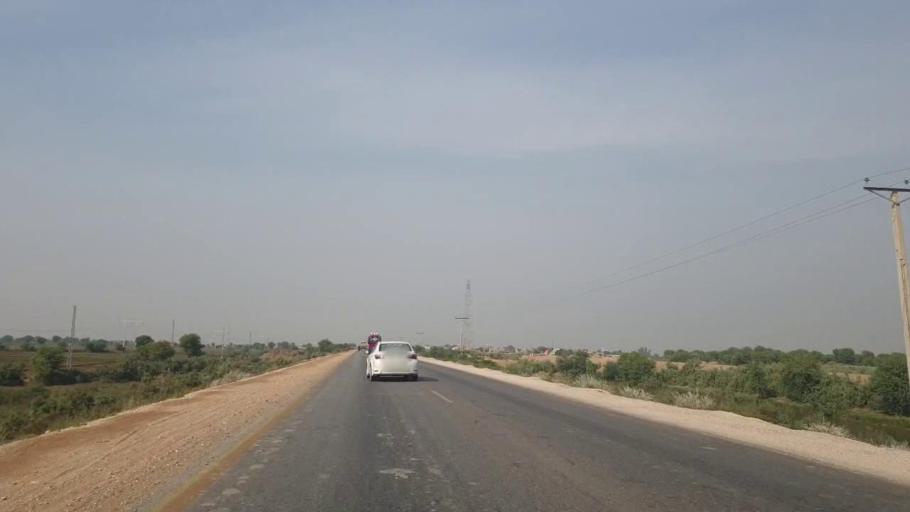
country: PK
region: Sindh
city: Sann
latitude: 26.0807
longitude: 68.0945
